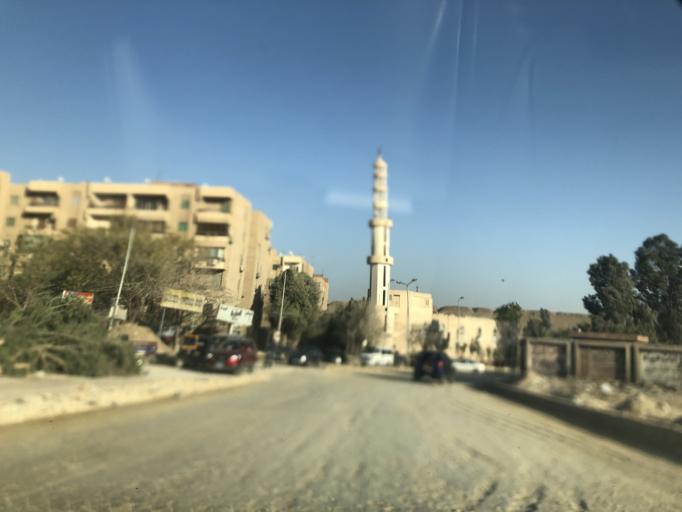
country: EG
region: Al Jizah
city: Al Jizah
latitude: 29.9833
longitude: 31.1123
